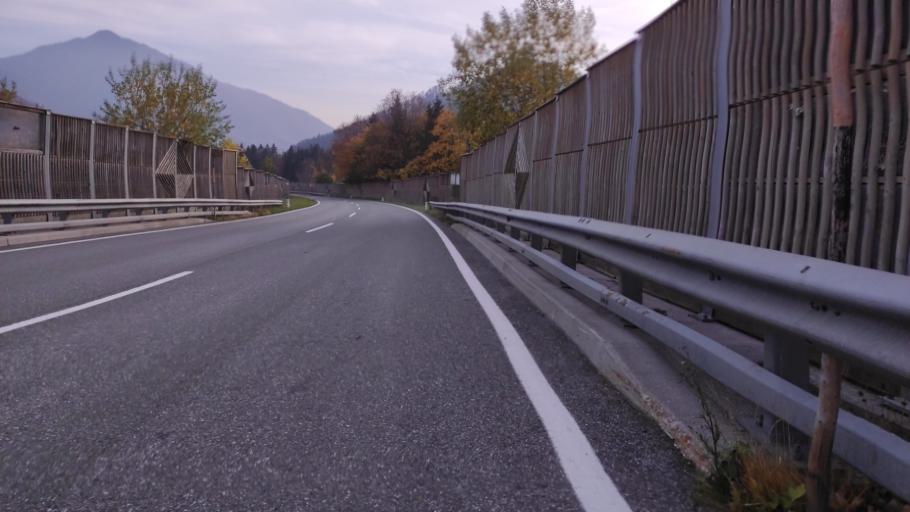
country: AT
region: Salzburg
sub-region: Politischer Bezirk Salzburg-Umgebung
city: Ebenau
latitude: 47.7921
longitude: 13.1734
